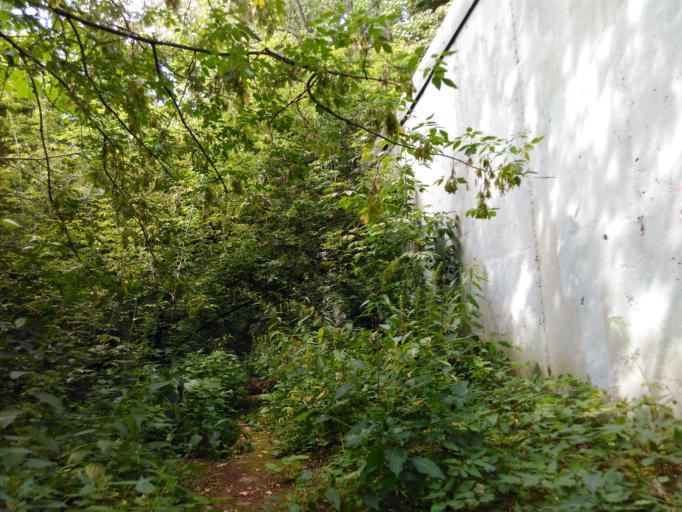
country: RU
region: Moskovskaya
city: Bol'shaya Setun'
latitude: 55.7143
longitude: 37.4183
